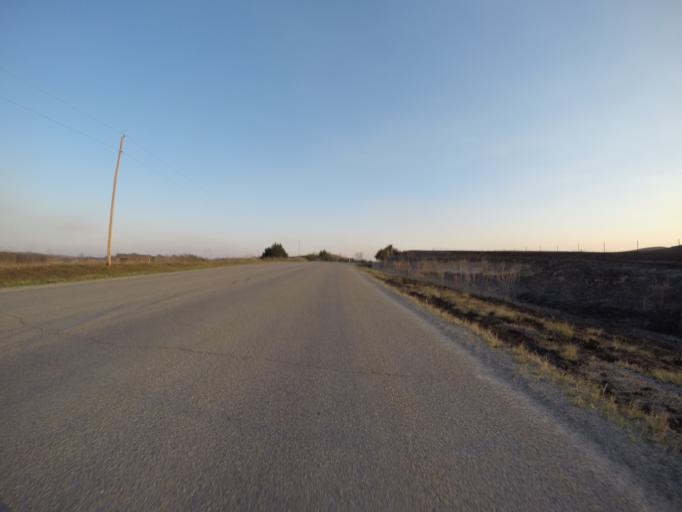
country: US
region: Kansas
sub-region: Riley County
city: Ogden
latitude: 39.0714
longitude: -96.6564
